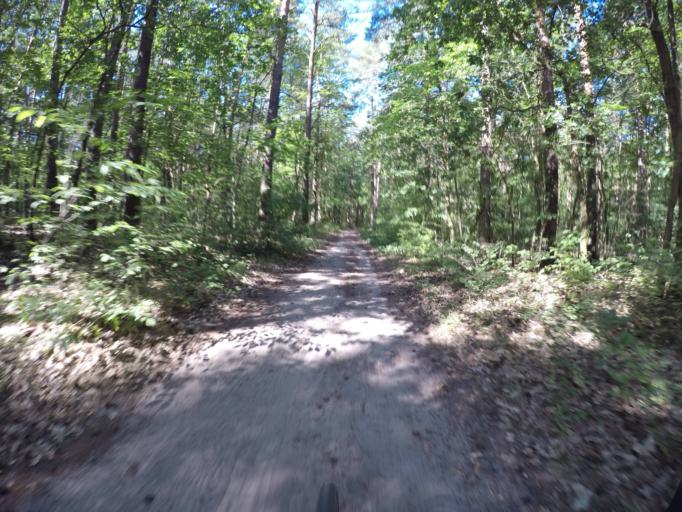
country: DE
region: Berlin
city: Rahnsdorf
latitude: 52.4522
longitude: 13.7077
